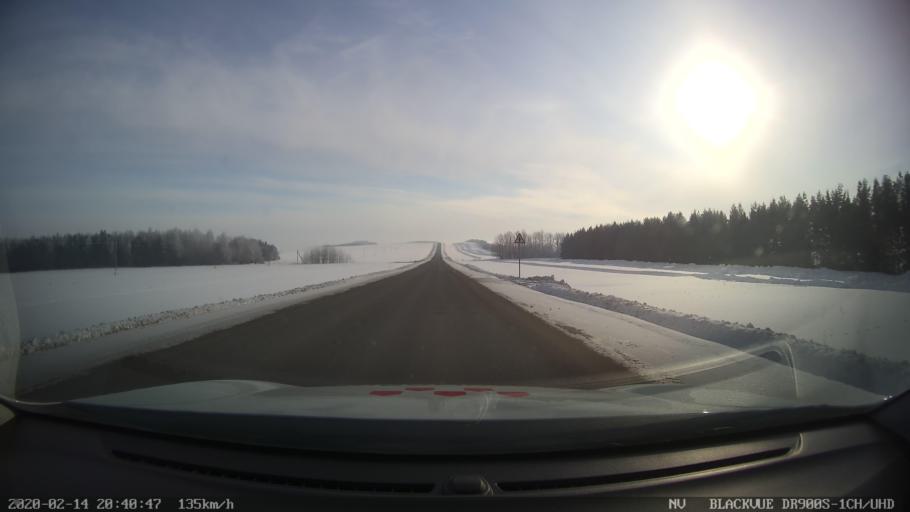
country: RU
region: Tatarstan
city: Kuybyshevskiy Zaton
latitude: 55.3368
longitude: 49.1006
